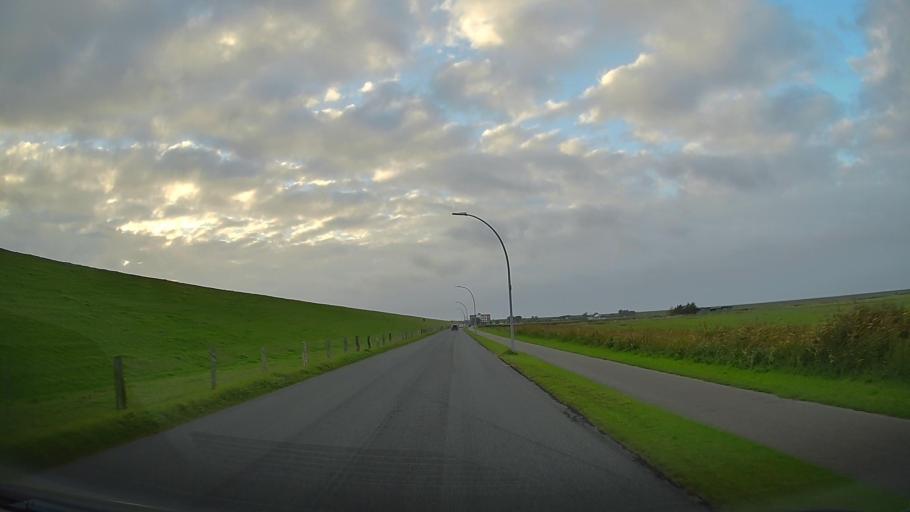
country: DE
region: Schleswig-Holstein
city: Husum
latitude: 54.4749
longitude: 9.0211
